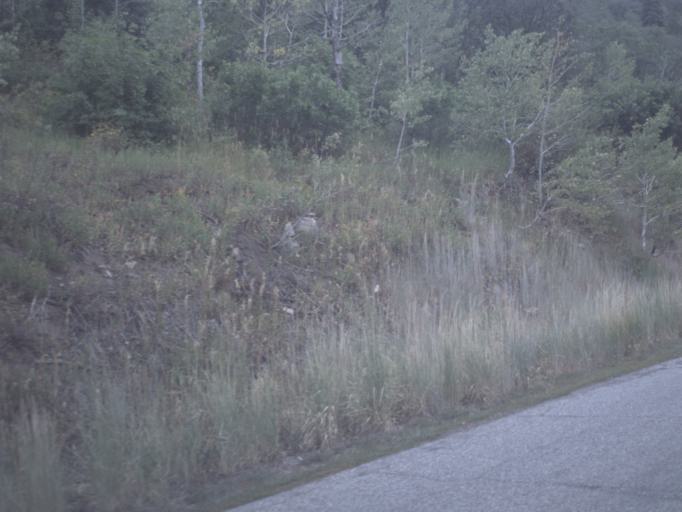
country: US
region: Utah
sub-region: Utah County
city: Lindon
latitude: 40.4038
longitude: -111.5980
